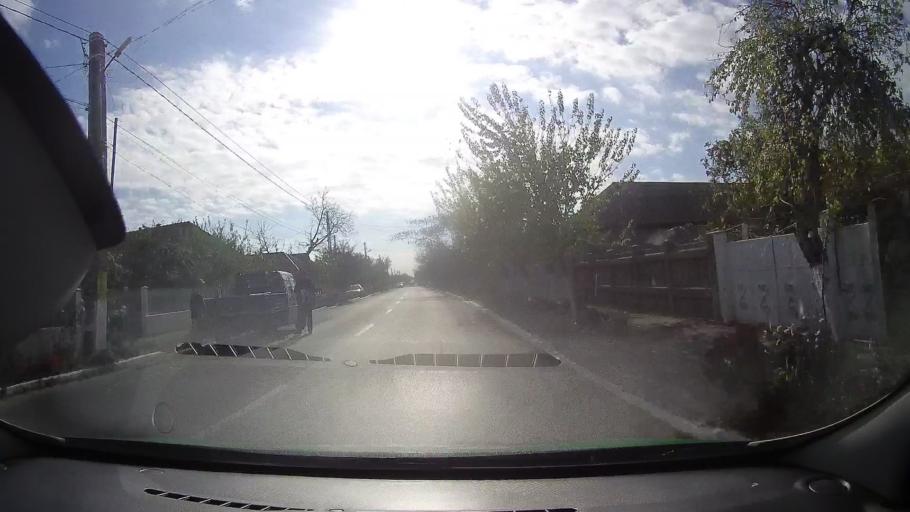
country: RO
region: Tulcea
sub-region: Comuna Sarichioi
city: Sarichioi
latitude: 44.9497
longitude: 28.8516
